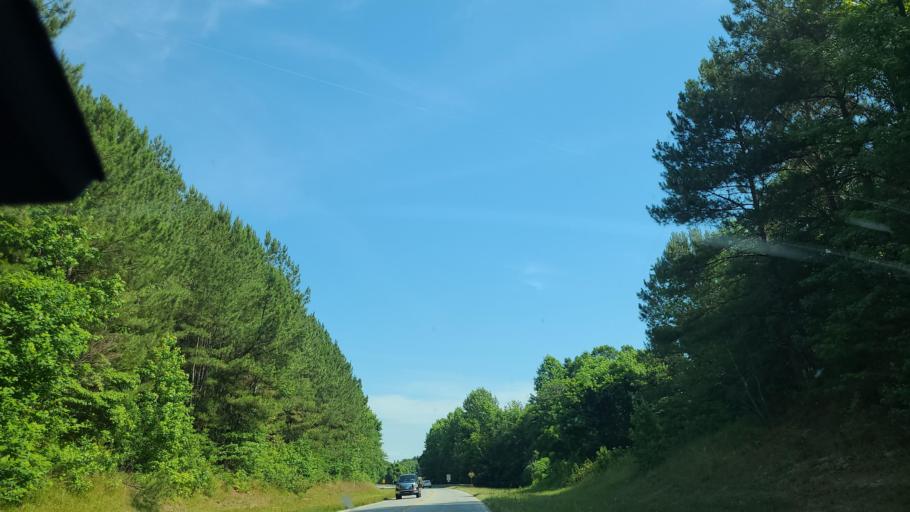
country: US
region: South Carolina
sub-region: Oconee County
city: Westminster
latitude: 34.6844
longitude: -83.0427
